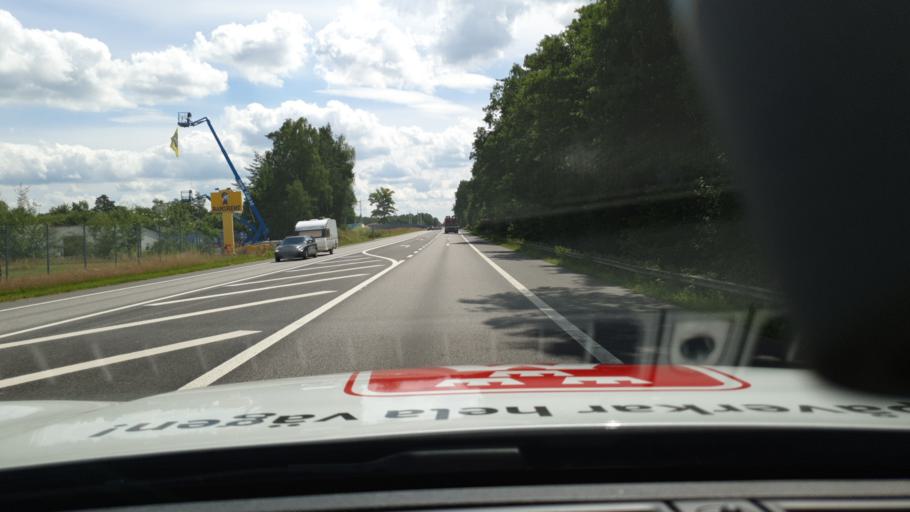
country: SE
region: Skane
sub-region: Hassleholms Kommun
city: Hassleholm
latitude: 56.1447
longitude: 13.7948
